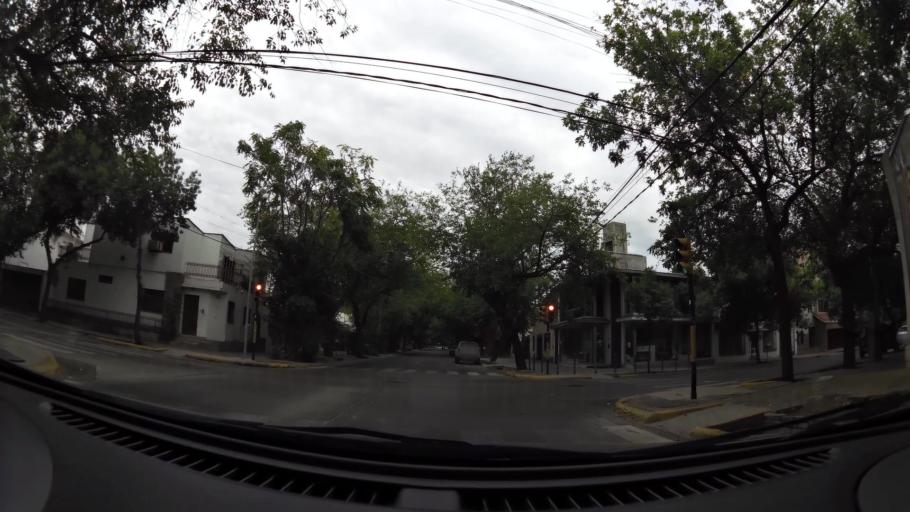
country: AR
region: Mendoza
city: Mendoza
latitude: -32.8985
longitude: -68.8637
